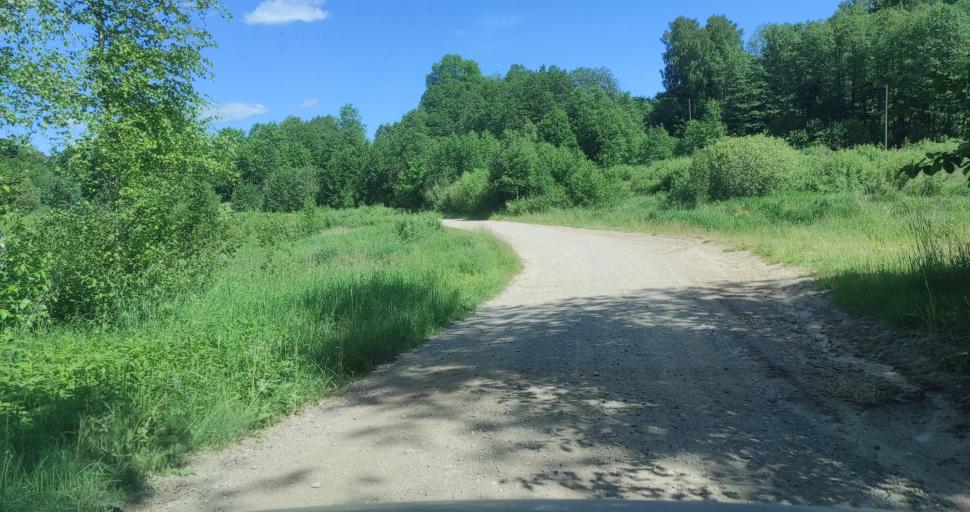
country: LV
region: Kuldigas Rajons
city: Kuldiga
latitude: 56.9338
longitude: 21.8292
